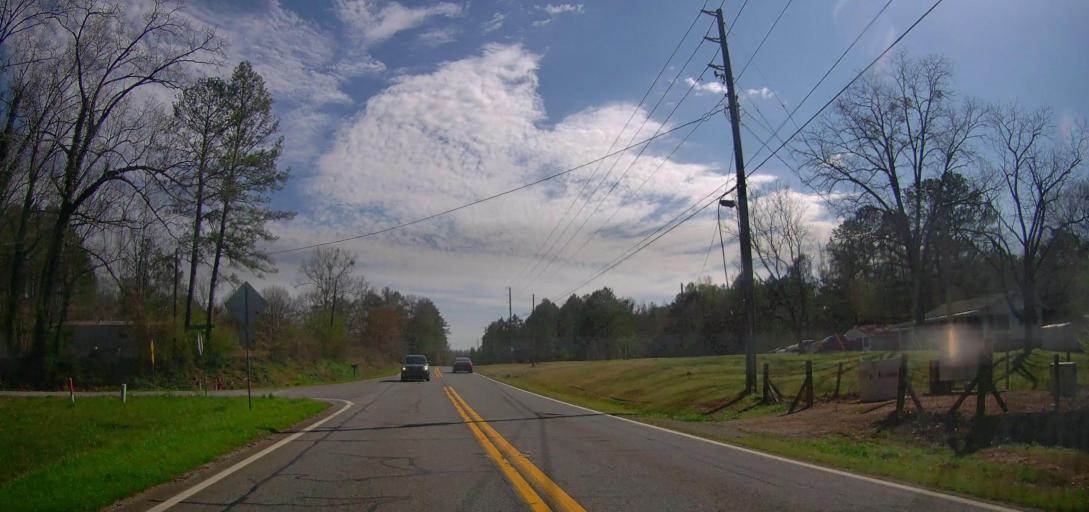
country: US
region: Georgia
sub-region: Monroe County
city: Forsyth
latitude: 33.1106
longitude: -83.9449
